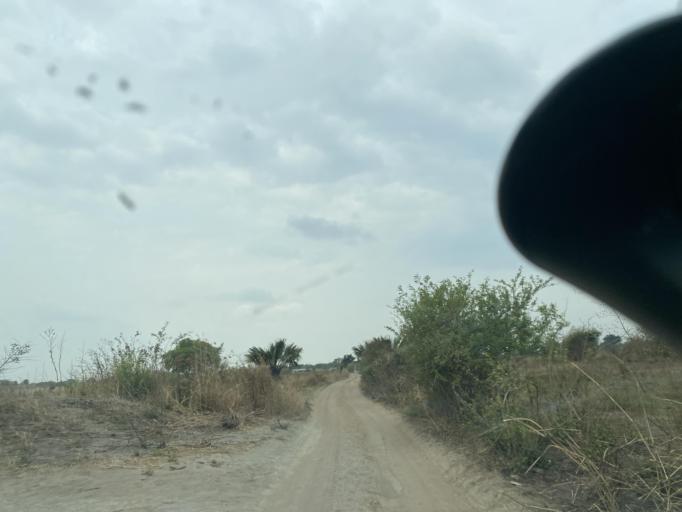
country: ZM
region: Lusaka
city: Lusaka
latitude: -15.2385
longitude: 28.3339
